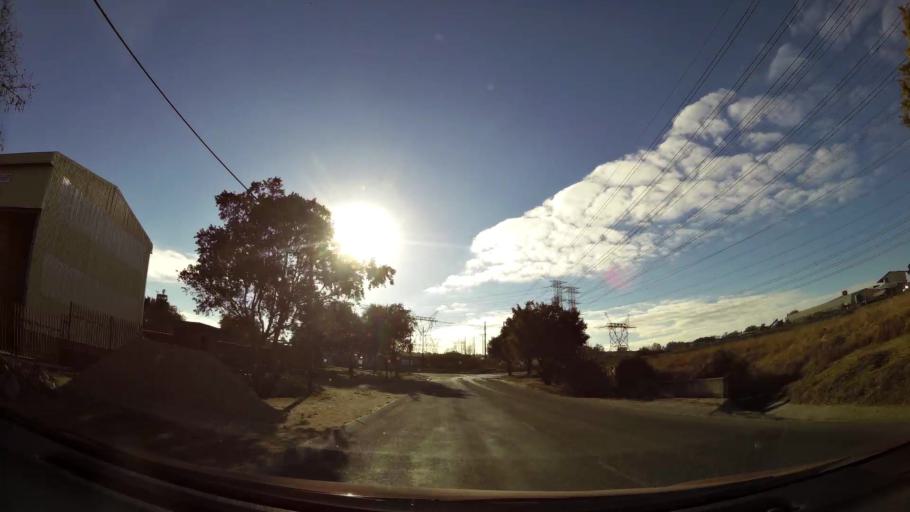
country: ZA
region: Gauteng
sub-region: City of Johannesburg Metropolitan Municipality
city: Modderfontein
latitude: -26.0378
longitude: 28.1591
